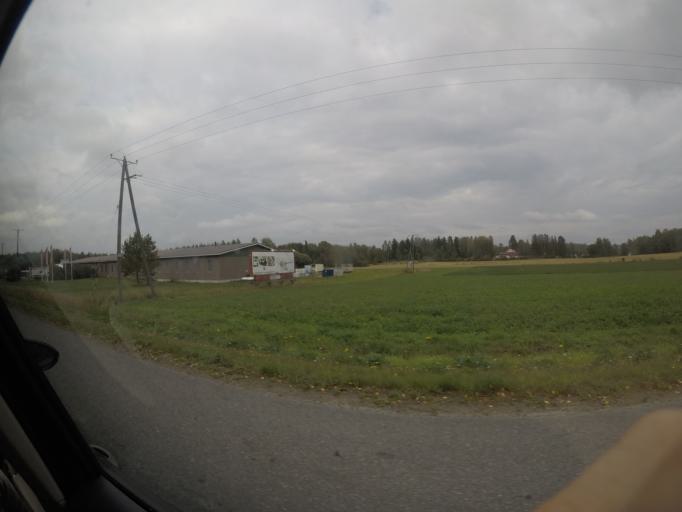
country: FI
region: Haeme
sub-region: Haemeenlinna
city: Parola
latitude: 61.0354
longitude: 24.4100
